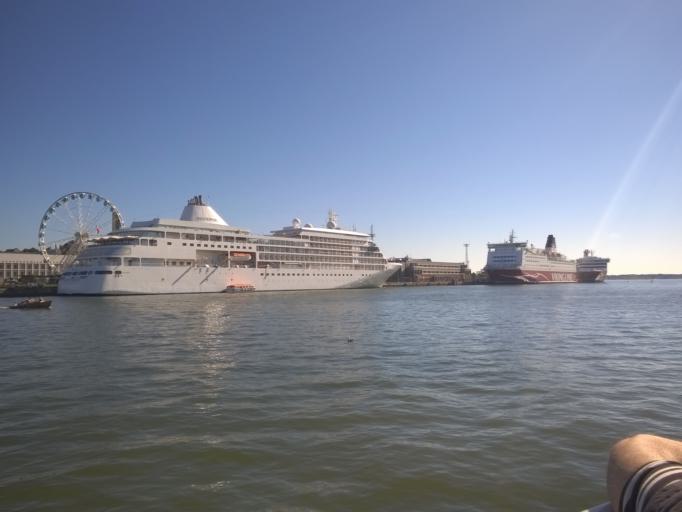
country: FI
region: Uusimaa
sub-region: Helsinki
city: Helsinki
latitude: 60.1655
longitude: 24.9558
